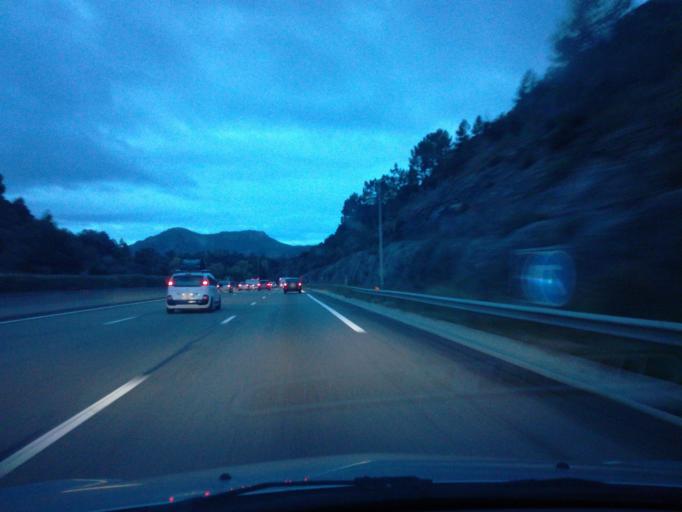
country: FR
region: Provence-Alpes-Cote d'Azur
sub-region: Departement du Var
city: Tanneron
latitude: 43.5403
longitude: 6.8374
